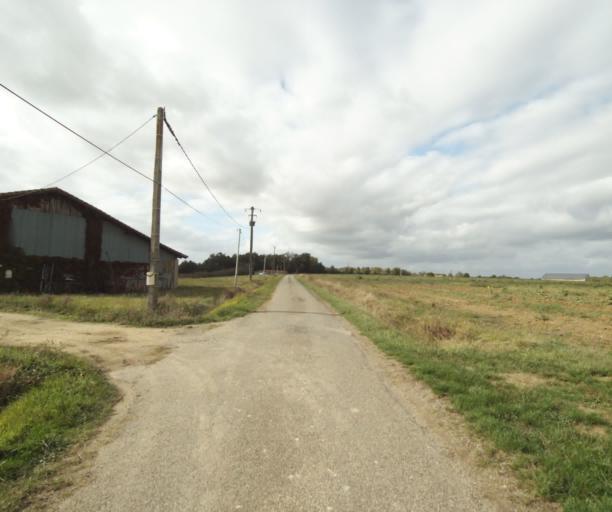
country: FR
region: Midi-Pyrenees
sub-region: Departement du Tarn-et-Garonne
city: Beaumont-de-Lomagne
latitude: 43.8840
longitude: 1.0841
